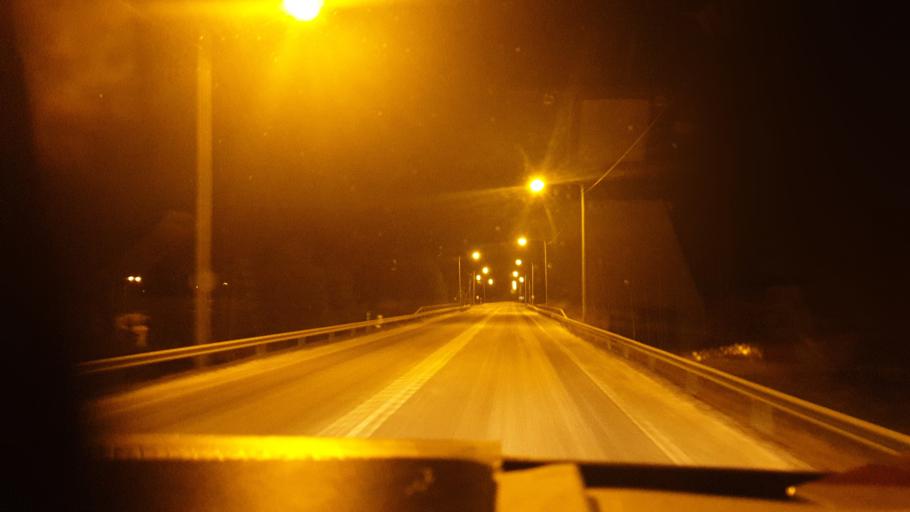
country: FI
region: Southern Ostrobothnia
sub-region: Kuusiokunnat
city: Alavus
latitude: 62.5964
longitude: 23.6627
